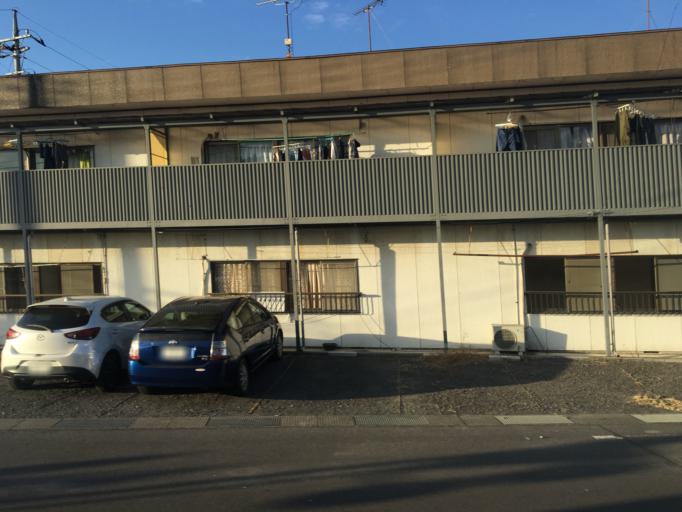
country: JP
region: Gunma
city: Isesaki
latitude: 36.3278
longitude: 139.2038
